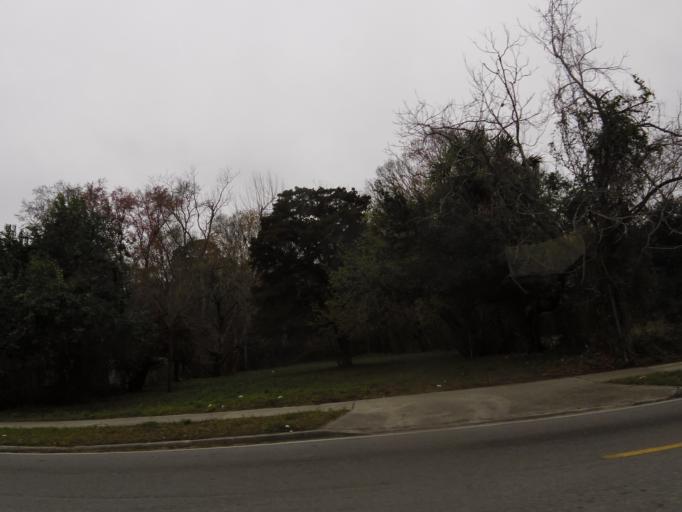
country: US
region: Florida
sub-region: Duval County
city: Jacksonville
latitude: 30.3732
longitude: -81.6990
